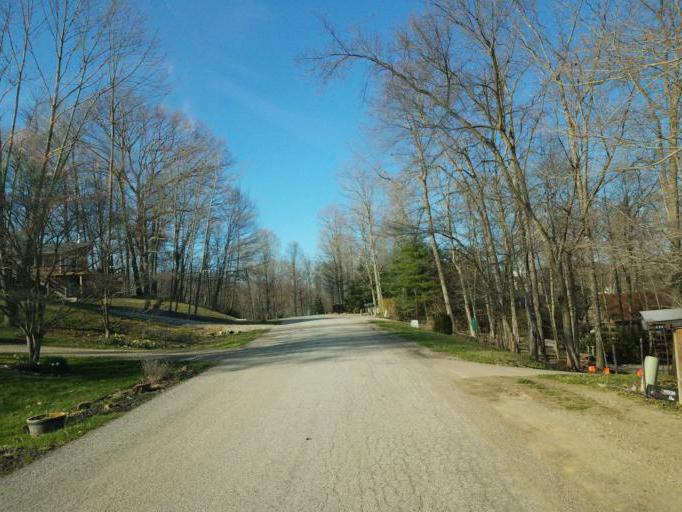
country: US
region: Ohio
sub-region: Knox County
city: Danville
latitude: 40.4488
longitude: -82.3420
